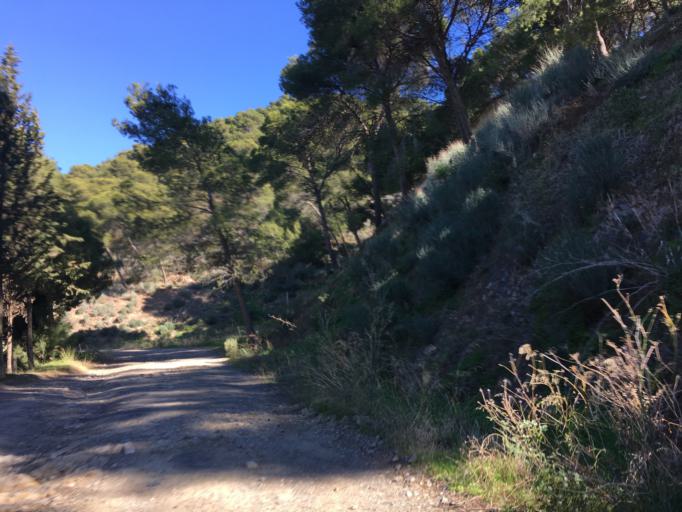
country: ES
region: Andalusia
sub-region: Provincia de Malaga
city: Malaga
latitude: 36.7780
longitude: -4.3851
